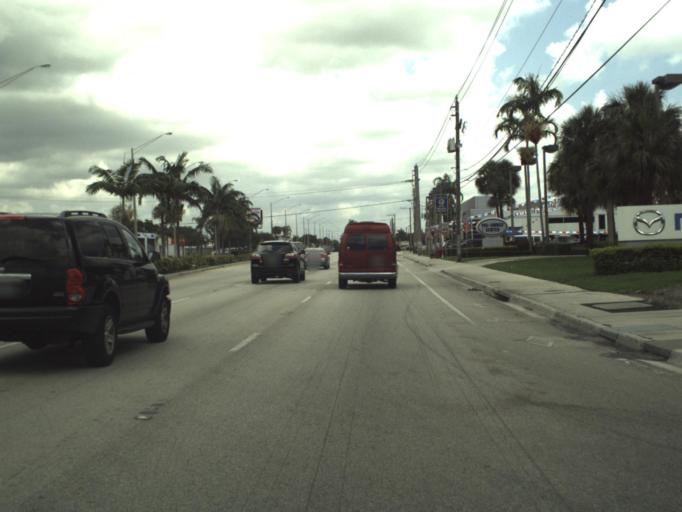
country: US
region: Florida
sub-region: Broward County
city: Broadview Park
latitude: 26.0978
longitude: -80.2011
